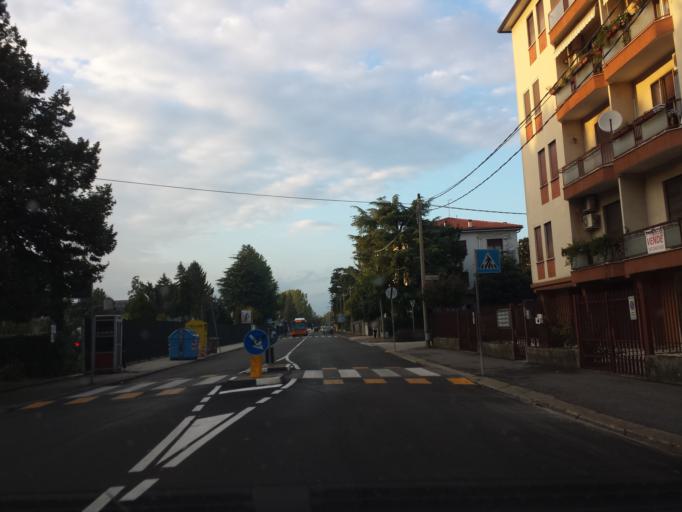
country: IT
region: Veneto
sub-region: Provincia di Vicenza
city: Vicenza
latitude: 45.5580
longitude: 11.5362
